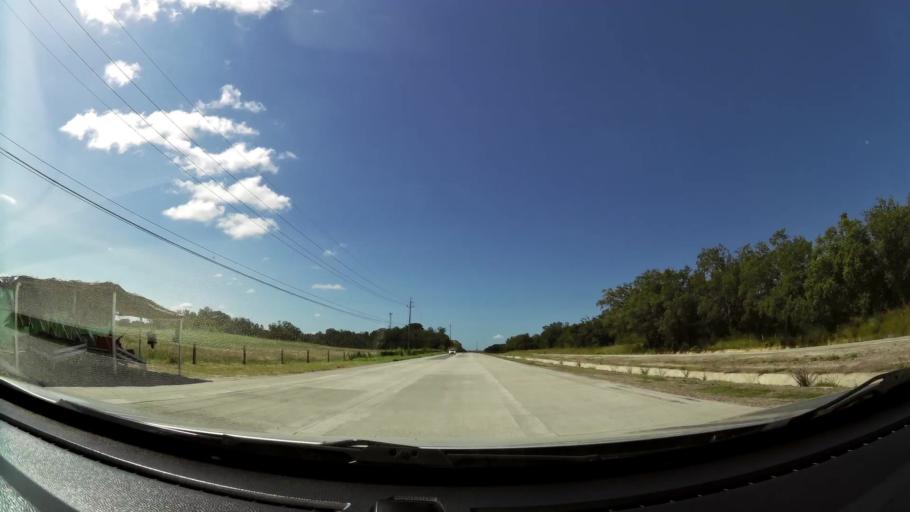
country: CR
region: Guanacaste
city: Bagaces
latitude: 10.5394
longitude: -85.3373
